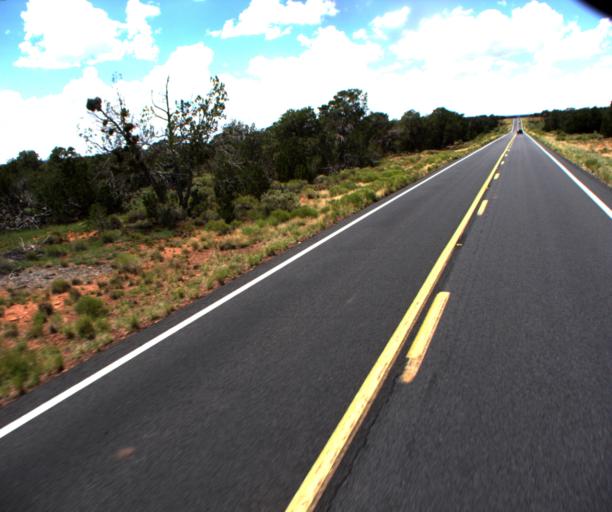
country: US
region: Arizona
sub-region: Coconino County
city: Parks
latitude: 35.5969
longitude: -112.0119
